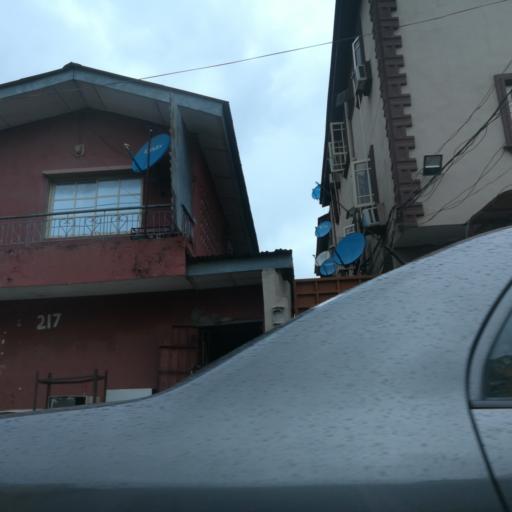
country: NG
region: Lagos
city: Makoko
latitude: 6.4918
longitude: 3.3798
